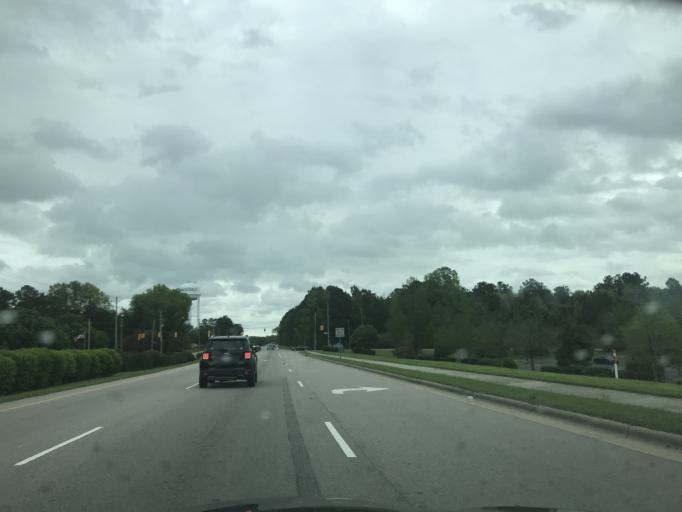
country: US
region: North Carolina
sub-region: Wake County
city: Knightdale
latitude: 35.7984
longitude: -78.4841
